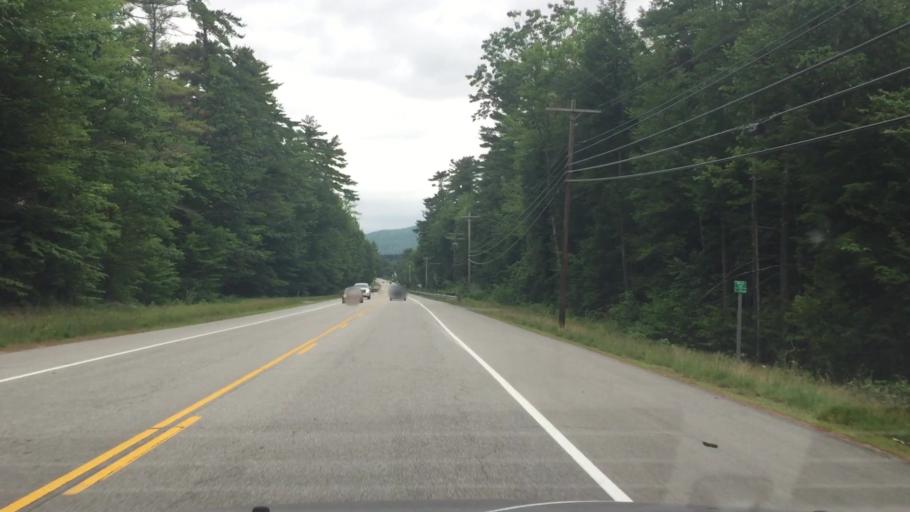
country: US
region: New Hampshire
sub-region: Carroll County
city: Center Harbor
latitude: 43.6947
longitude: -71.4593
